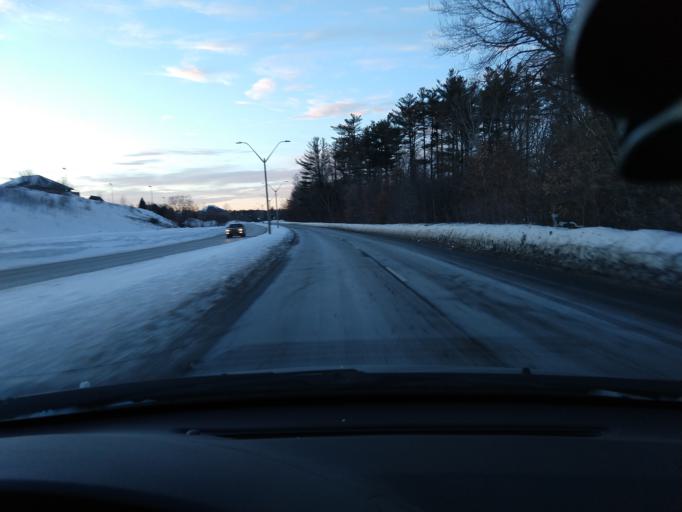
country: US
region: Massachusetts
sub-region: Middlesex County
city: Pinehurst
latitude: 42.4963
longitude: -71.2275
